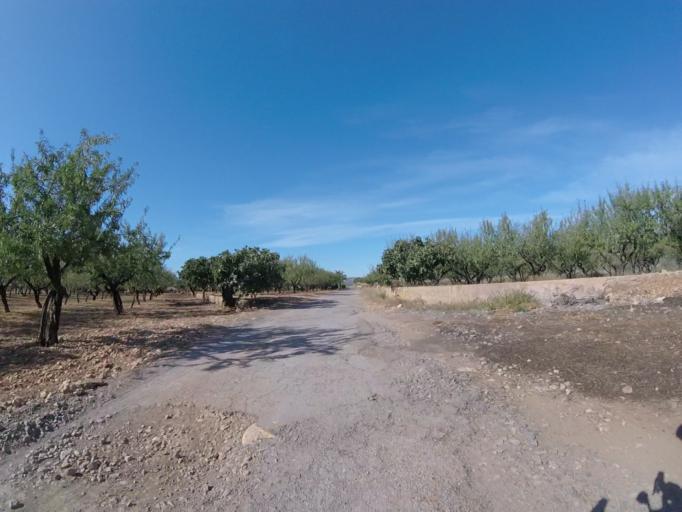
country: ES
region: Valencia
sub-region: Provincia de Castello
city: Torreblanca
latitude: 40.2102
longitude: 0.2296
